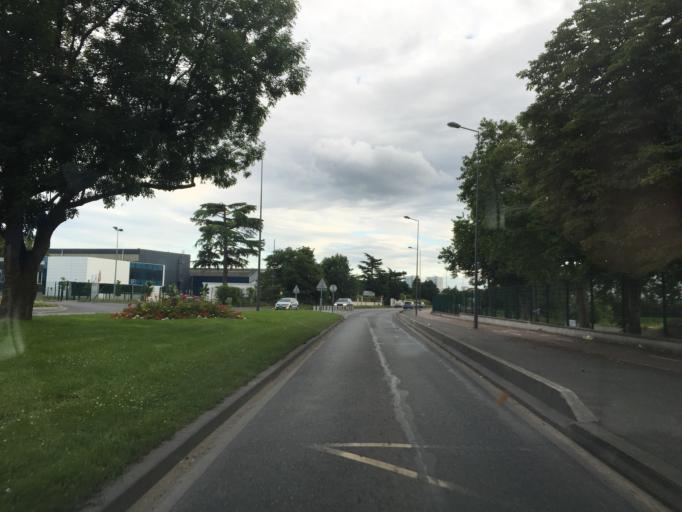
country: FR
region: Ile-de-France
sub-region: Departement du Val-de-Marne
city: Saint-Maur-des-Fosses
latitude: 48.7817
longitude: 2.4942
